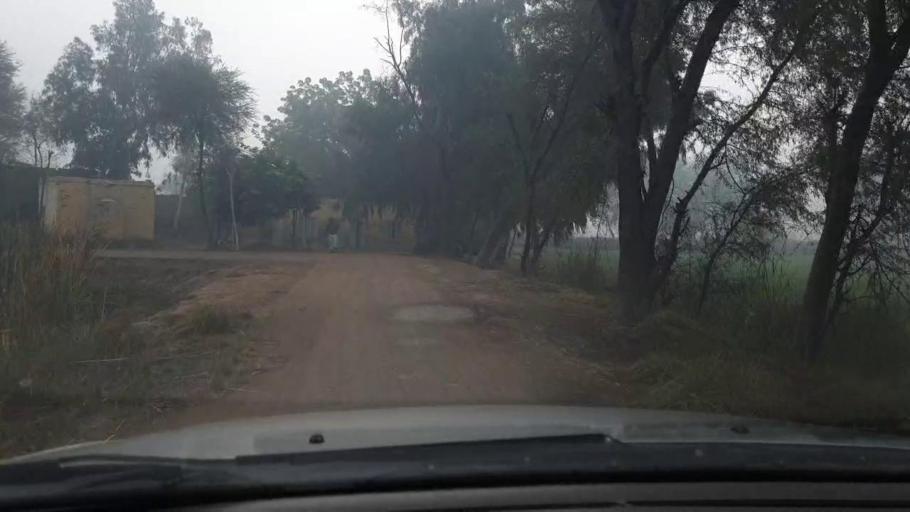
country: PK
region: Sindh
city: Mirpur Mathelo
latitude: 27.9280
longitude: 69.5188
